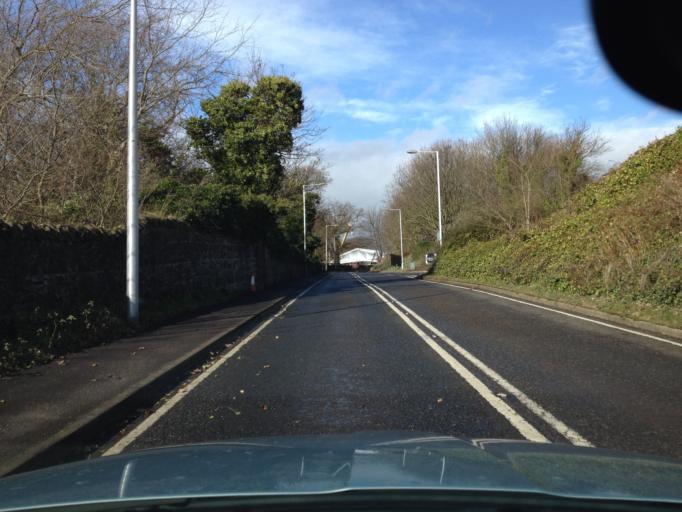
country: GB
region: Scotland
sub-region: Fife
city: North Queensferry
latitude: 56.0123
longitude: -3.4055
